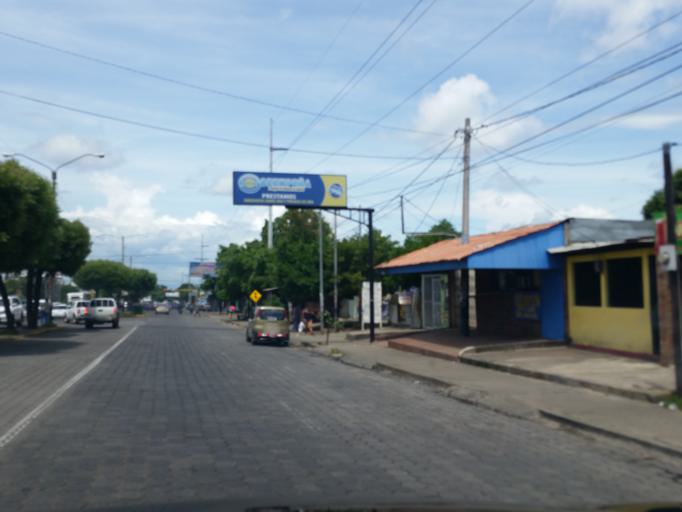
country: NI
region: Managua
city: Managua
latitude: 12.1242
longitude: -86.2415
